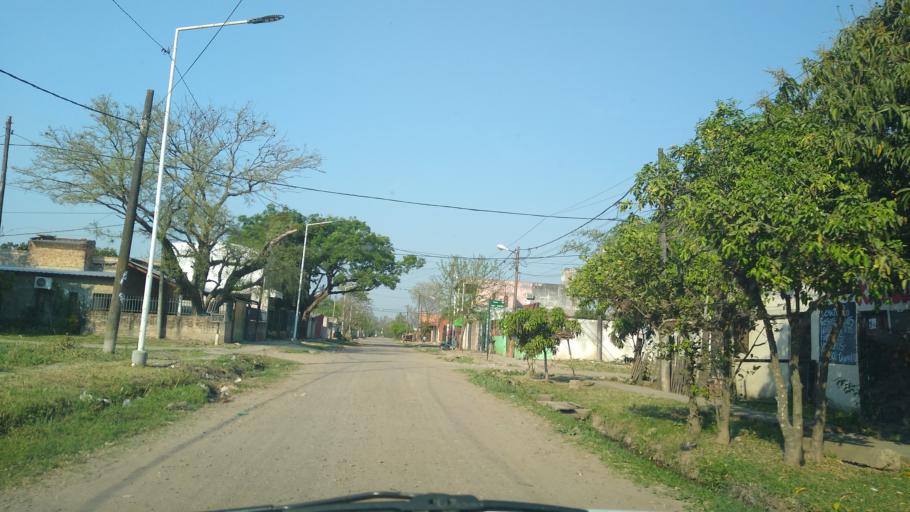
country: AR
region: Chaco
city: Barranqueras
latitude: -27.4743
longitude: -58.9482
